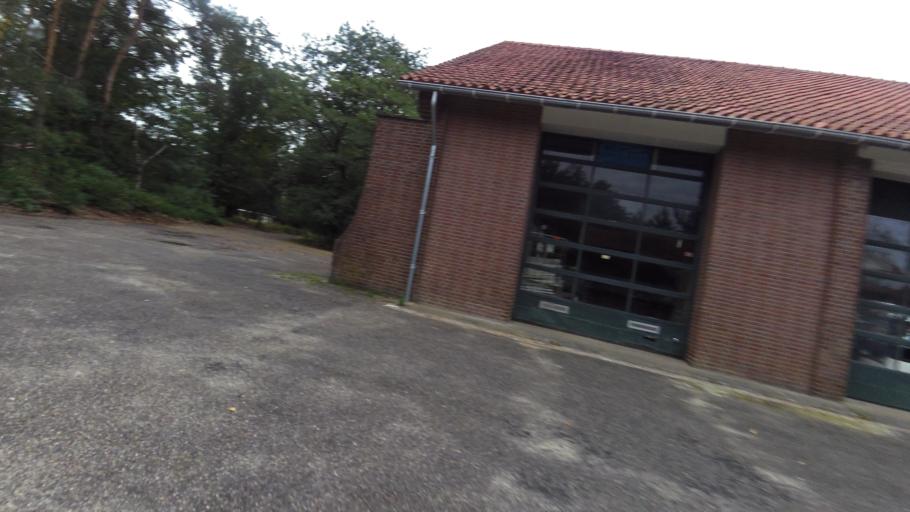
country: NL
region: Gelderland
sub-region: Gemeente Ede
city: Harskamp
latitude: 52.1751
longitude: 5.8245
